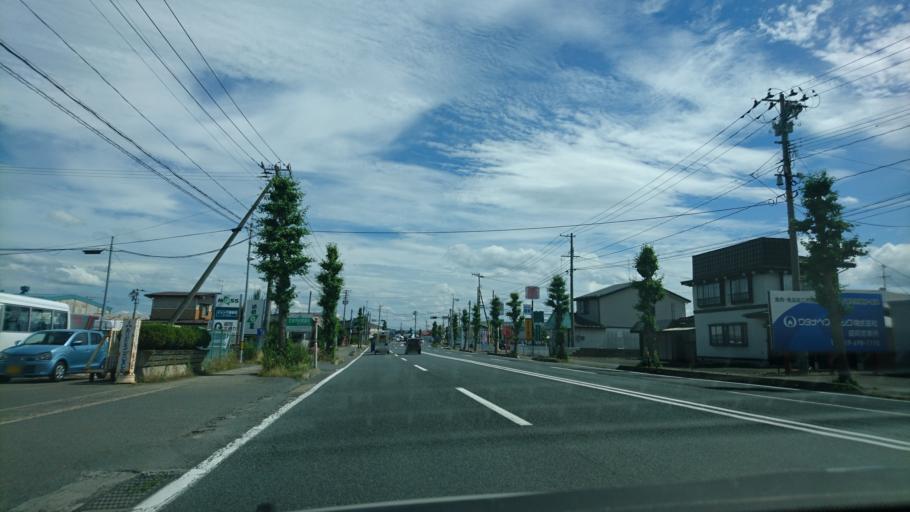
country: JP
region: Iwate
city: Morioka-shi
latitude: 39.6286
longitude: 141.1744
